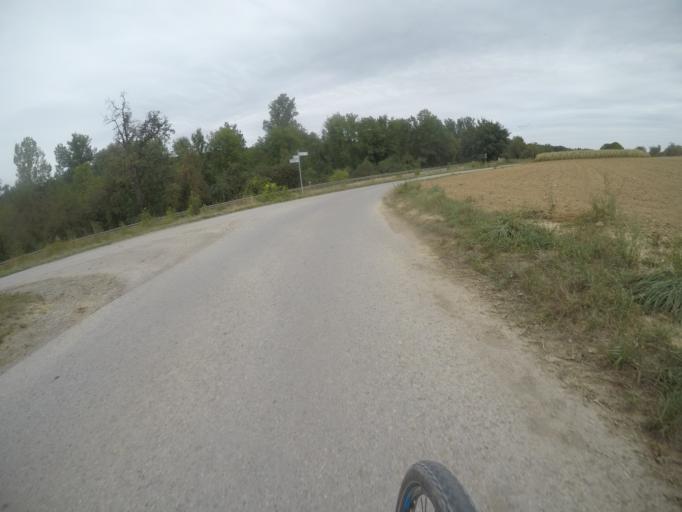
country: DE
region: Baden-Wuerttemberg
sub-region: Regierungsbezirk Stuttgart
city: Oberriexingen
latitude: 48.9303
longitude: 9.0387
